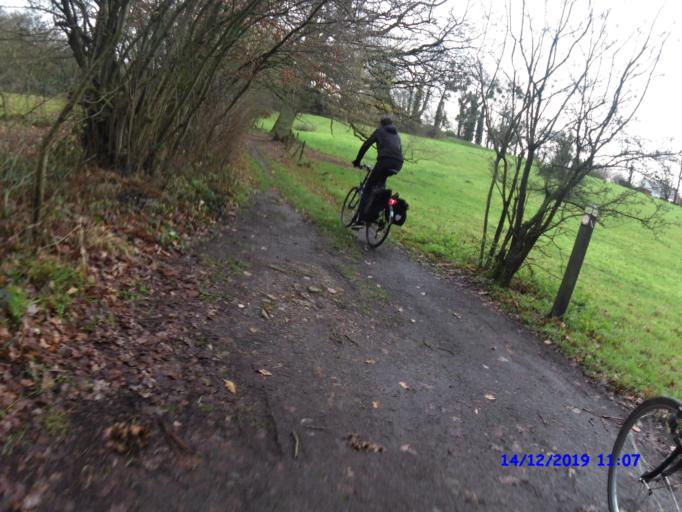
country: BE
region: Flanders
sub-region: Provincie Vlaams-Brabant
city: Beersel
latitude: 50.7518
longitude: 4.3093
